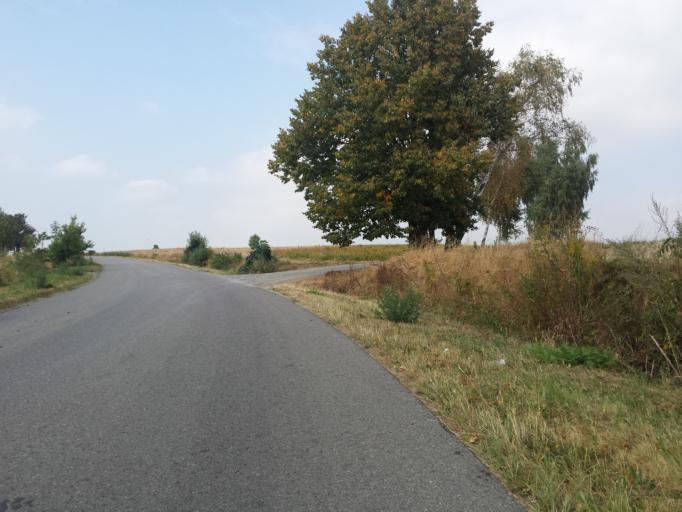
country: PL
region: Subcarpathian Voivodeship
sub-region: Powiat brzozowski
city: Wesola
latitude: 49.8403
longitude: 22.1520
